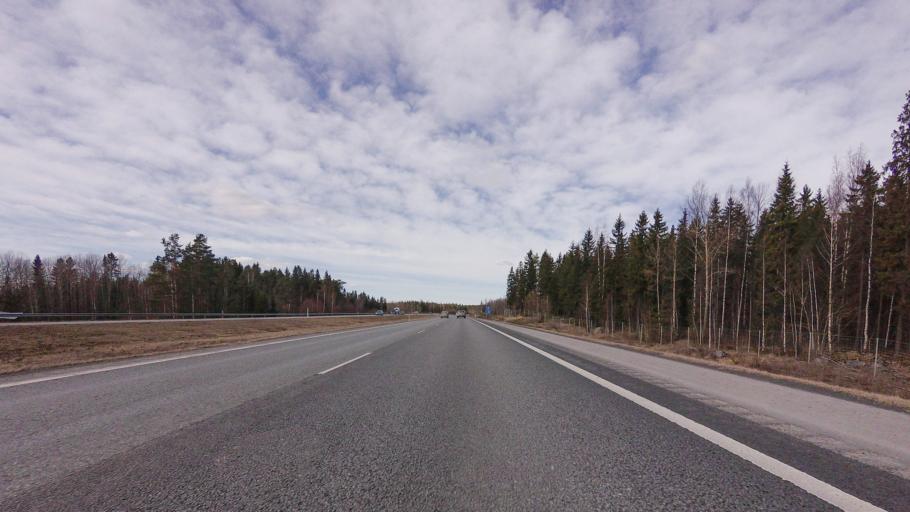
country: FI
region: Pirkanmaa
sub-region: Etelae-Pirkanmaa
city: Viiala
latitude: 61.2697
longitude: 23.8211
